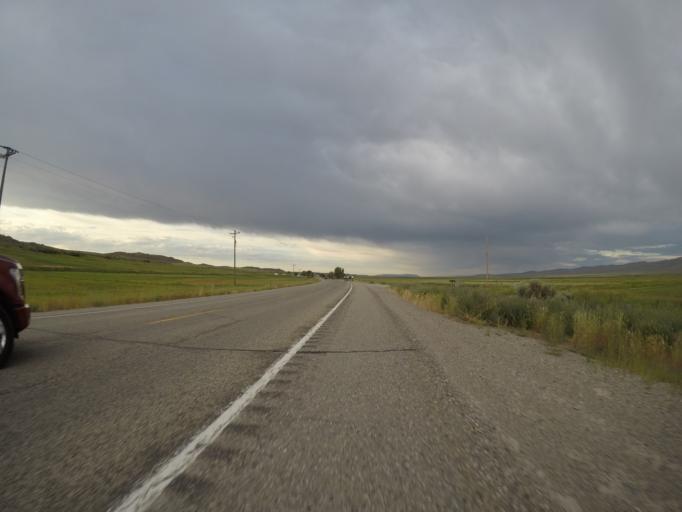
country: US
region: Utah
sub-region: Rich County
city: Randolph
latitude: 42.0349
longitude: -110.9324
